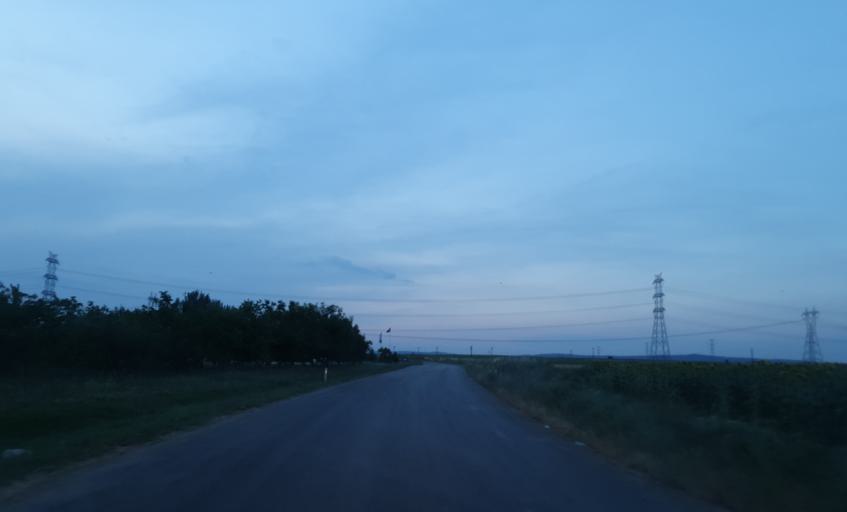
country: TR
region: Kirklareli
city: Vize
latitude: 41.4915
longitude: 27.7519
